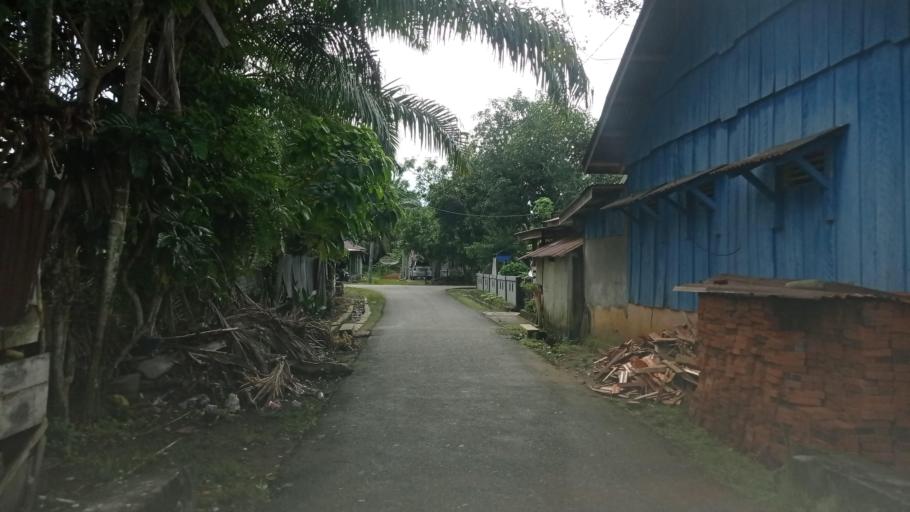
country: ID
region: Bengkulu
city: Ipuh
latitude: -2.5765
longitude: 101.1175
